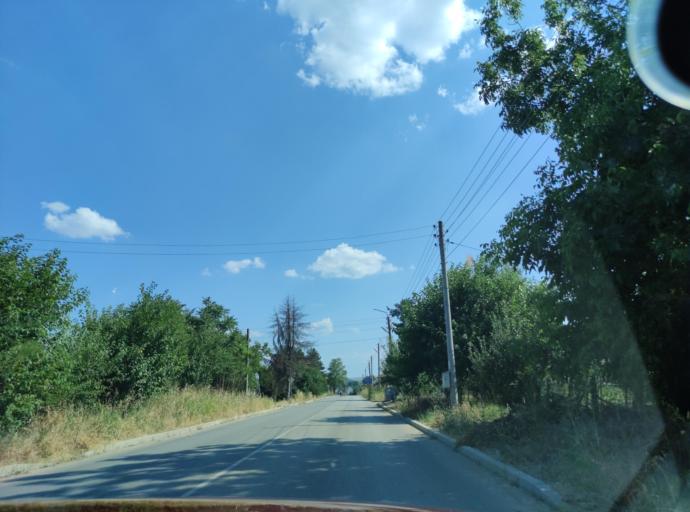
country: BG
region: Pleven
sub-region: Obshtina Cherven Bryag
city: Koynare
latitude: 43.3325
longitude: 24.0667
